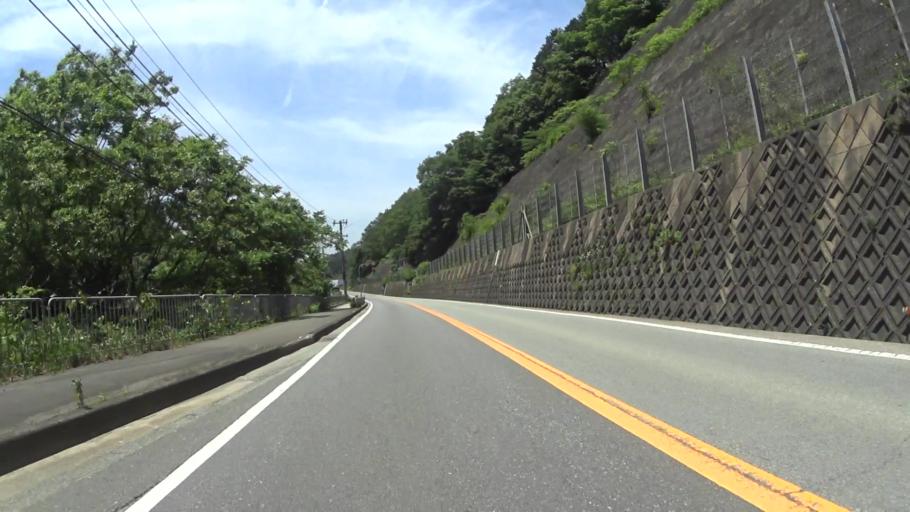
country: JP
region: Kyoto
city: Ayabe
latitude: 35.1782
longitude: 135.3936
